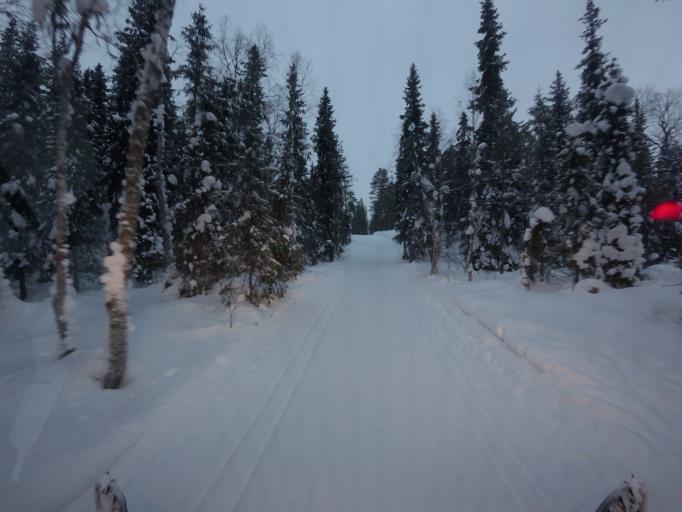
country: FI
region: Lapland
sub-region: Tunturi-Lappi
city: Kolari
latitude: 67.6187
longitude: 24.1685
